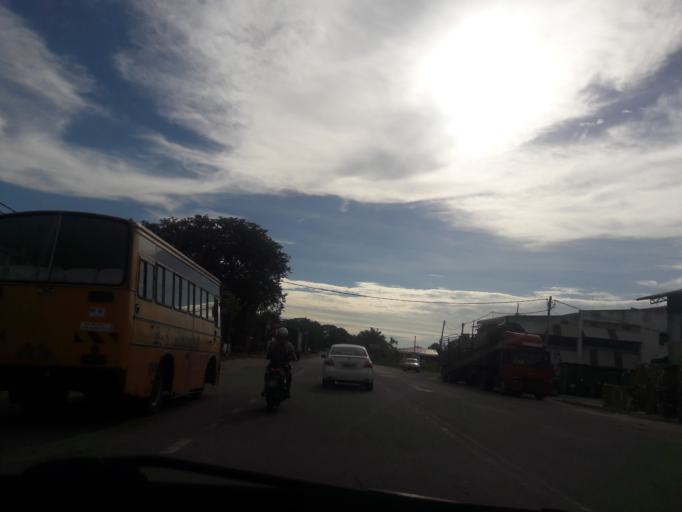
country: MY
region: Kedah
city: Sungai Petani
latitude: 5.6347
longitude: 100.5076
